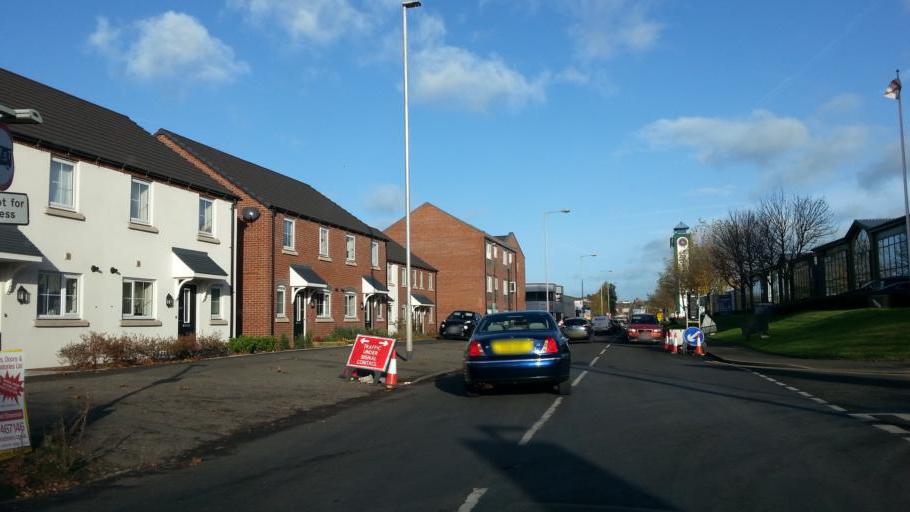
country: GB
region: England
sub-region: Staffordshire
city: Cannock
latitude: 52.6755
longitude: -2.0252
